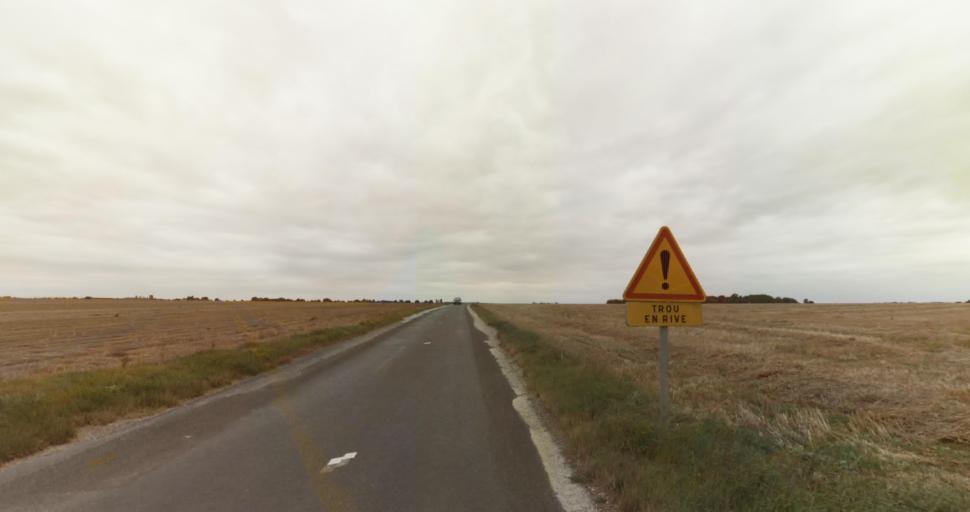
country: FR
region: Haute-Normandie
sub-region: Departement de l'Eure
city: Evreux
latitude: 48.9600
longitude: 1.2400
